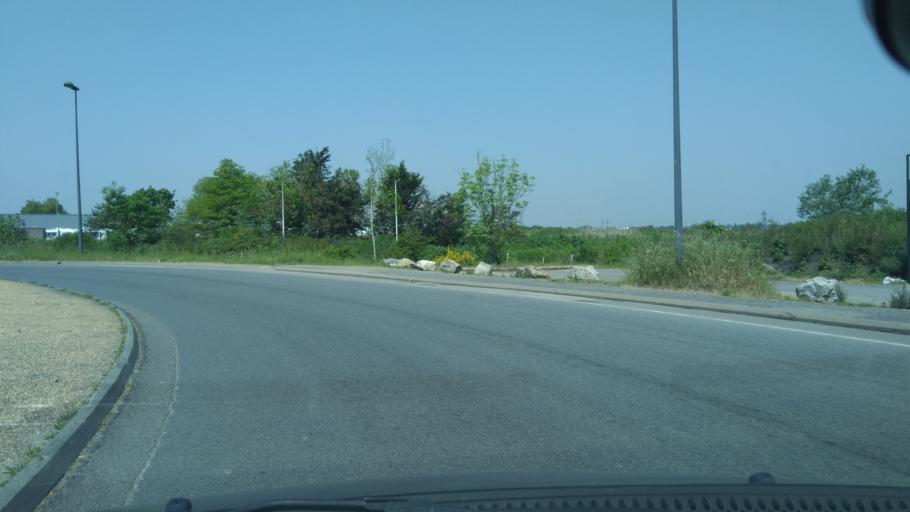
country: FR
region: Pays de la Loire
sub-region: Departement de la Loire-Atlantique
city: Montoir-de-Bretagne
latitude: 47.3266
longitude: -2.1624
